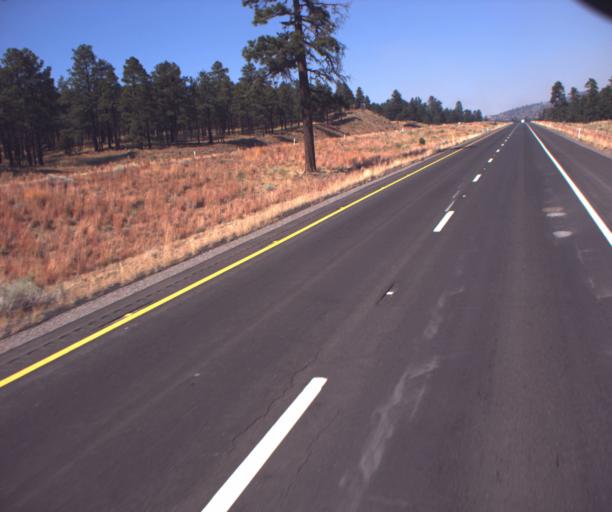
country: US
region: Arizona
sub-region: Coconino County
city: Flagstaff
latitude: 35.3550
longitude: -111.5694
